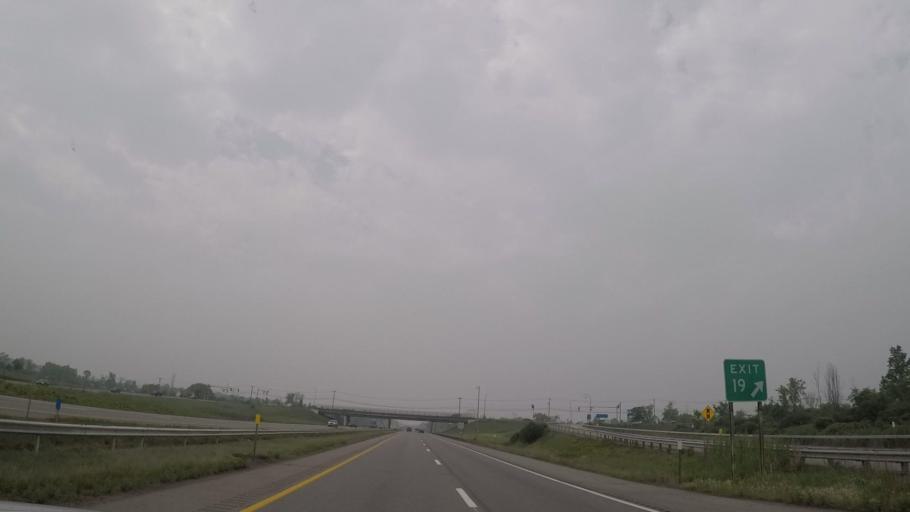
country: US
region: New York
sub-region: Erie County
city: Grandyle Village
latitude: 43.0199
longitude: -78.9732
